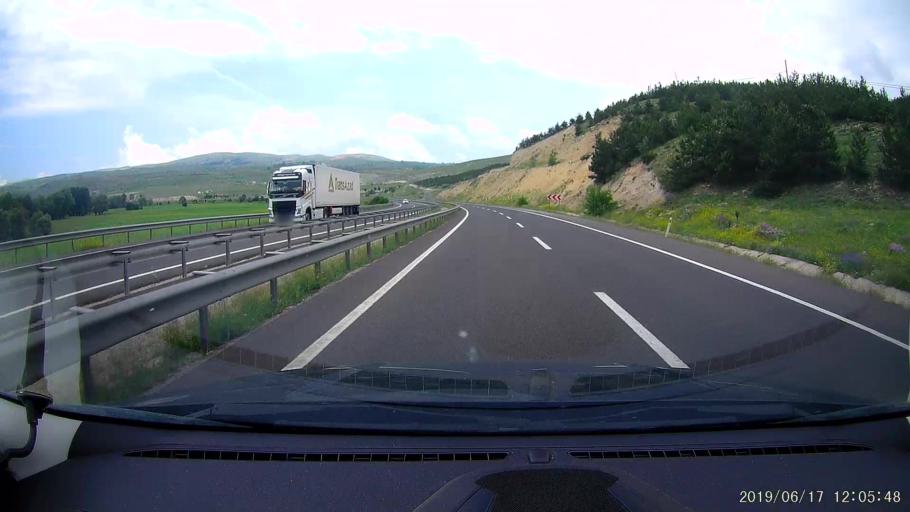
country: TR
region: Cankiri
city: Cerkes
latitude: 40.8366
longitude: 32.7726
